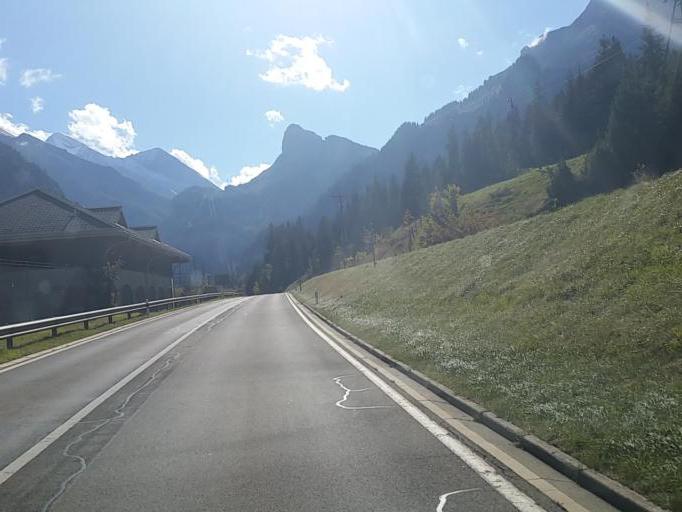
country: CH
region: Bern
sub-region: Frutigen-Niedersimmental District
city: Kandersteg
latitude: 46.5031
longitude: 7.6744
